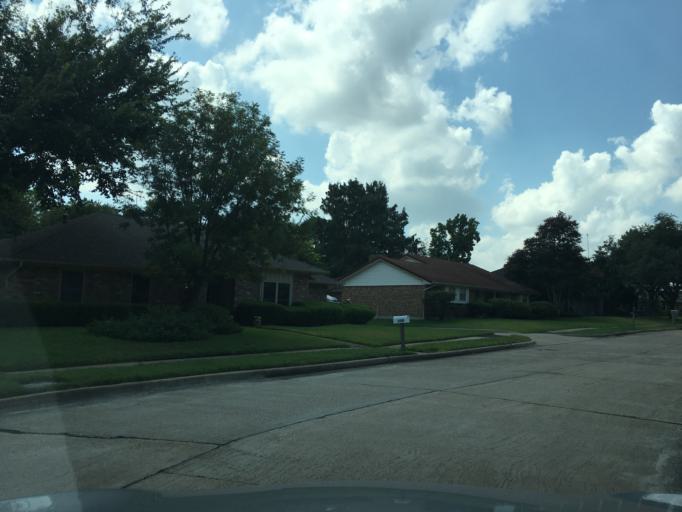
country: US
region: Texas
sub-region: Dallas County
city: Garland
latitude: 32.9431
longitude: -96.6386
